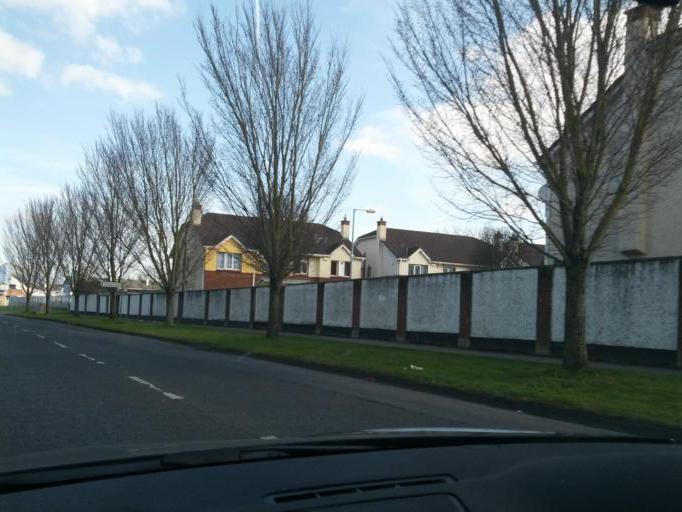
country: IE
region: Leinster
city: Clondalkin
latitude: 53.3392
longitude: -6.4225
